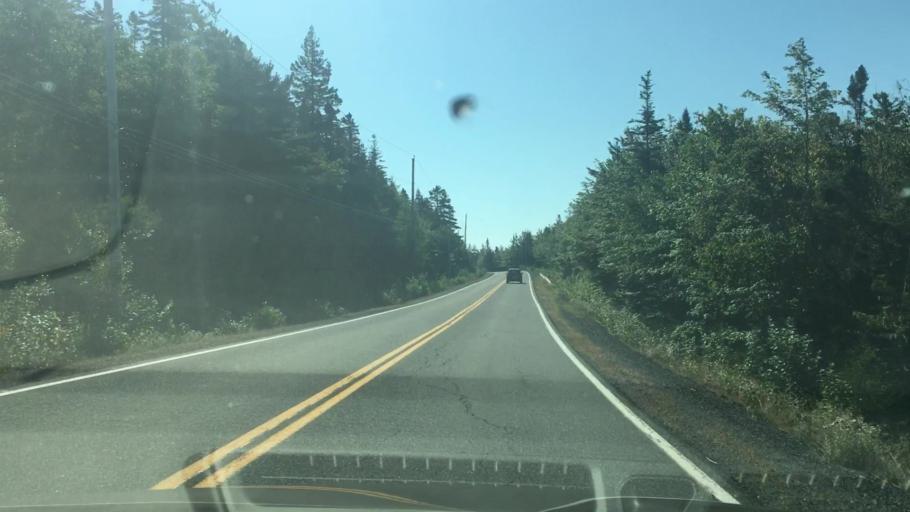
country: CA
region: Nova Scotia
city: Cole Harbour
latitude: 44.8101
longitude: -62.8354
